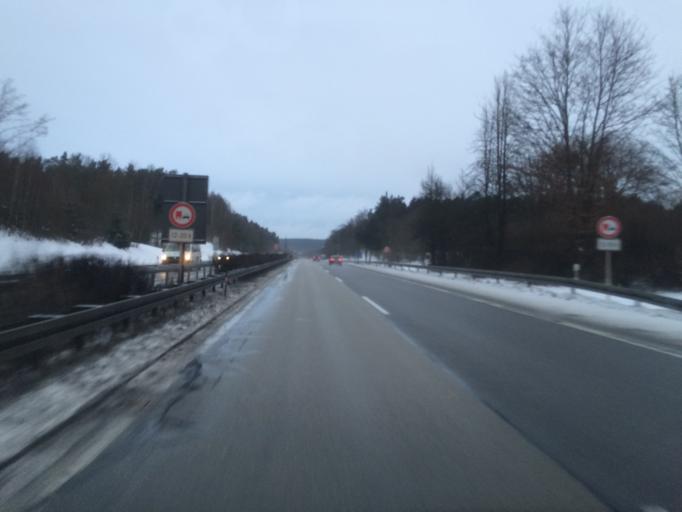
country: DE
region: Bavaria
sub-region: Upper Palatinate
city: Zeitlarn
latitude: 49.0878
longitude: 12.0981
